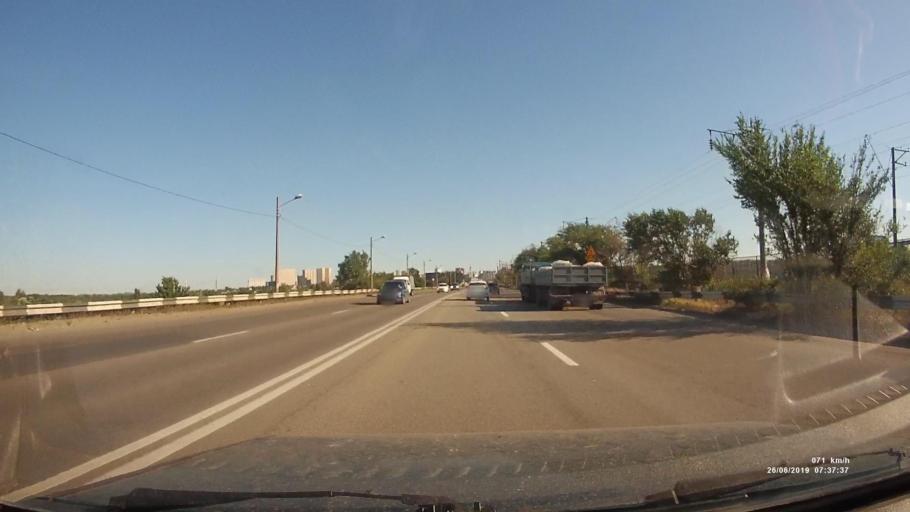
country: RU
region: Rostov
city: Rostov-na-Donu
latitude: 47.1780
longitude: 39.6403
